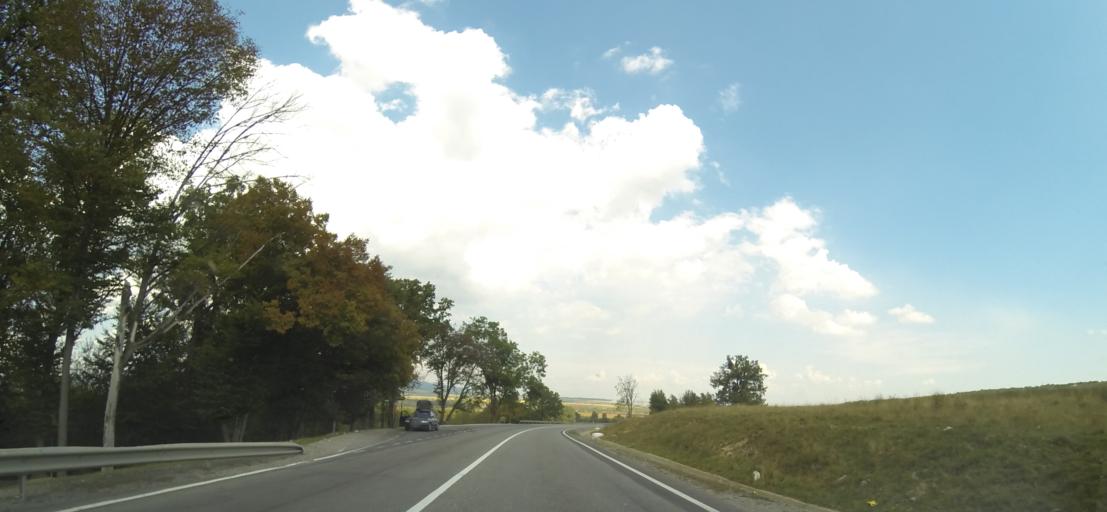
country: RO
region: Brasov
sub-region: Comuna Dumbravita
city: Dumbravita
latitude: 45.7537
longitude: 25.3960
